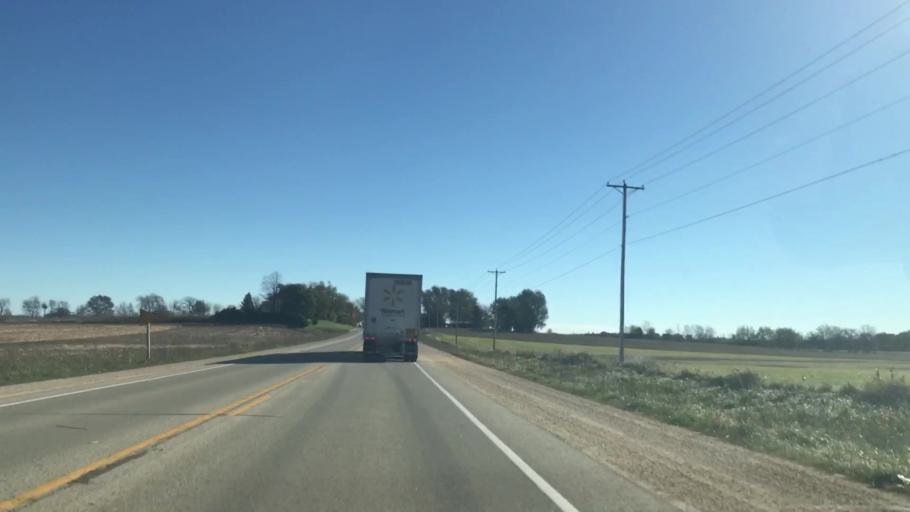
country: US
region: Wisconsin
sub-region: Dodge County
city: Horicon
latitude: 43.4445
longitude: -88.6702
